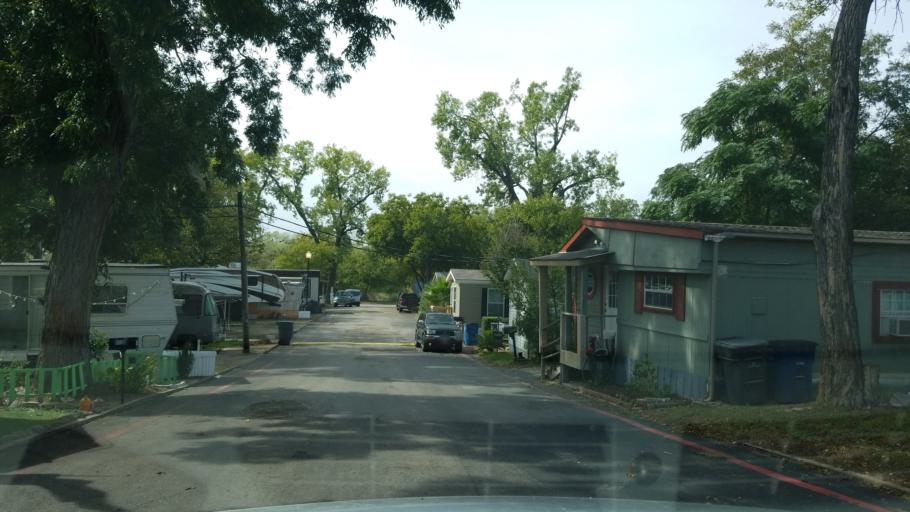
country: US
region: Texas
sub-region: Dallas County
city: Highland Park
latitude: 32.7880
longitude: -96.7230
